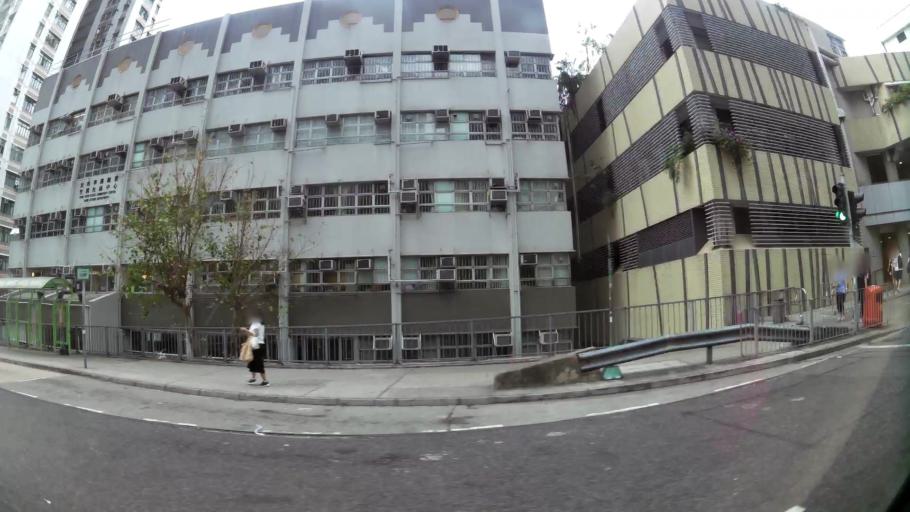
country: HK
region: Wong Tai Sin
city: Wong Tai Sin
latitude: 22.3451
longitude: 114.1937
